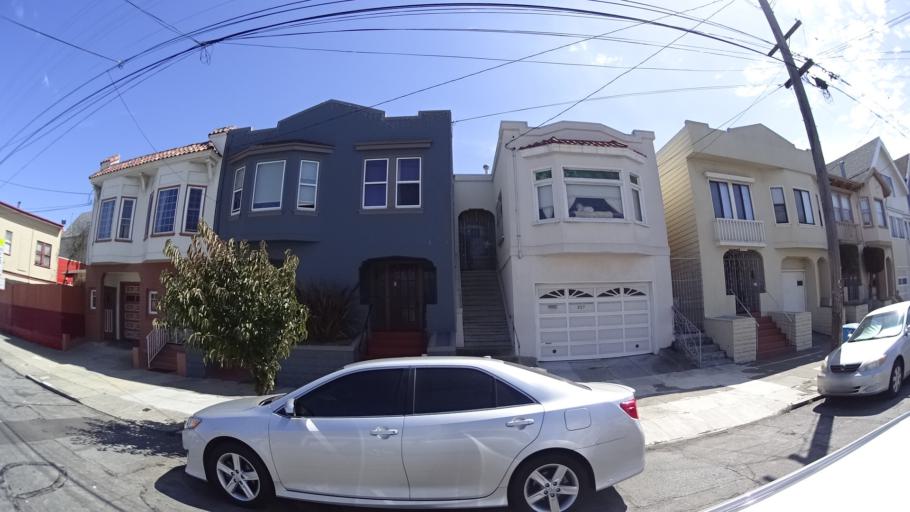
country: US
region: California
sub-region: San Mateo County
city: Daly City
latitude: 37.7253
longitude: -122.4333
